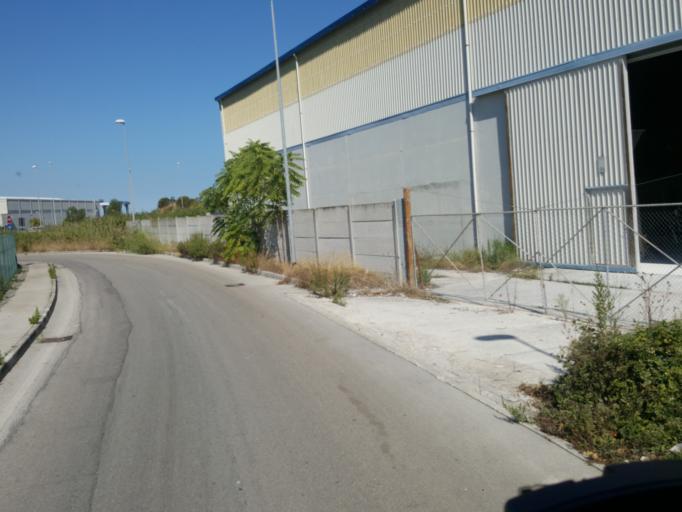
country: IT
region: The Marches
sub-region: Provincia di Ancona
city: Posatora
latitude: 43.6111
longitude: 13.4976
